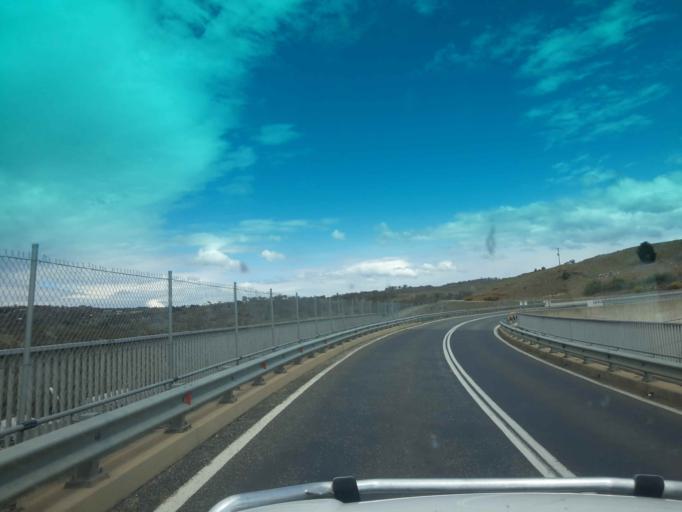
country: AU
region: New South Wales
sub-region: Snowy River
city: Jindabyne
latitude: -36.4345
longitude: 148.6330
